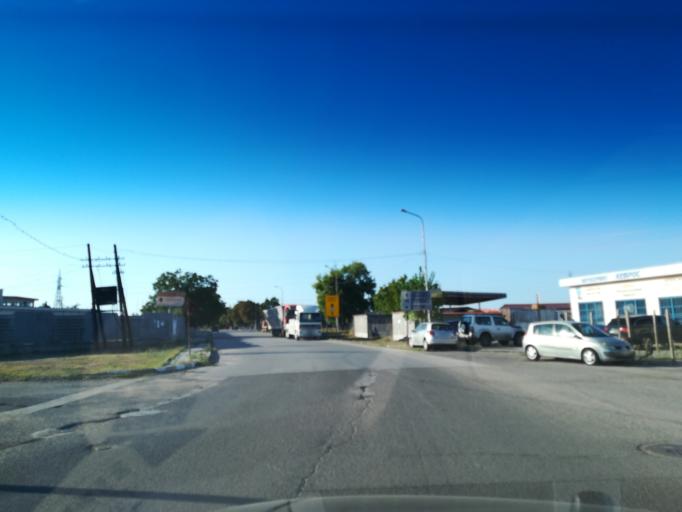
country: BG
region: Stara Zagora
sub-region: Obshtina Chirpan
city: Chirpan
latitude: 42.1071
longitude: 25.2215
